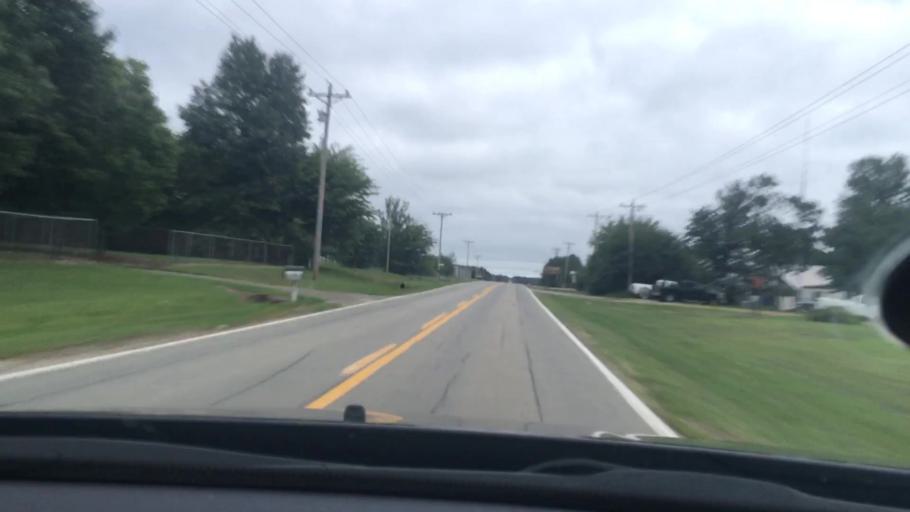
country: US
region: Oklahoma
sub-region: Sequoyah County
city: Vian
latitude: 35.6097
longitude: -94.9919
